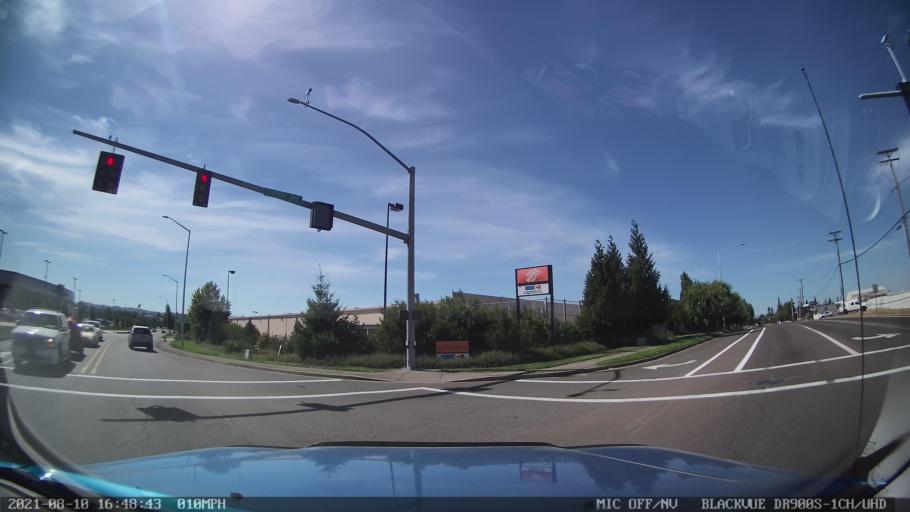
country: US
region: Oregon
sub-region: Marion County
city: Keizer
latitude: 44.9695
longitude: -123.0202
